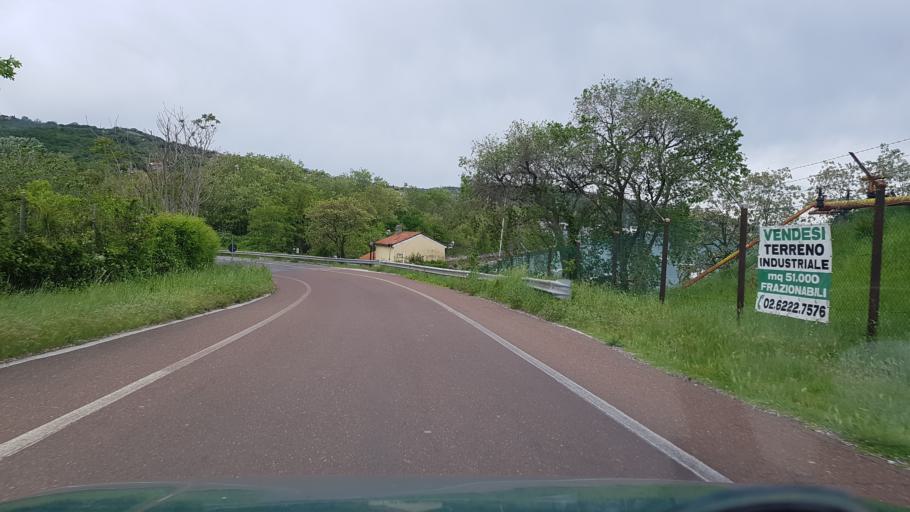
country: IT
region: Friuli Venezia Giulia
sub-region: Provincia di Trieste
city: Muggia
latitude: 45.6012
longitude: 13.7916
